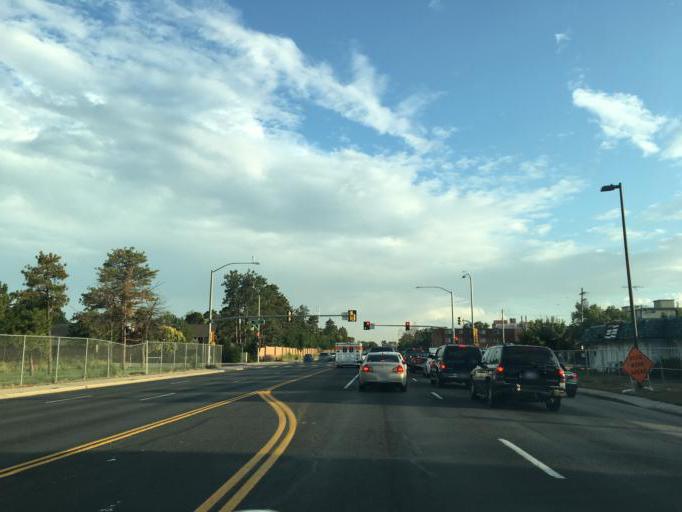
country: US
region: Colorado
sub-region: Adams County
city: Aurora
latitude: 39.7446
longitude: -104.8470
